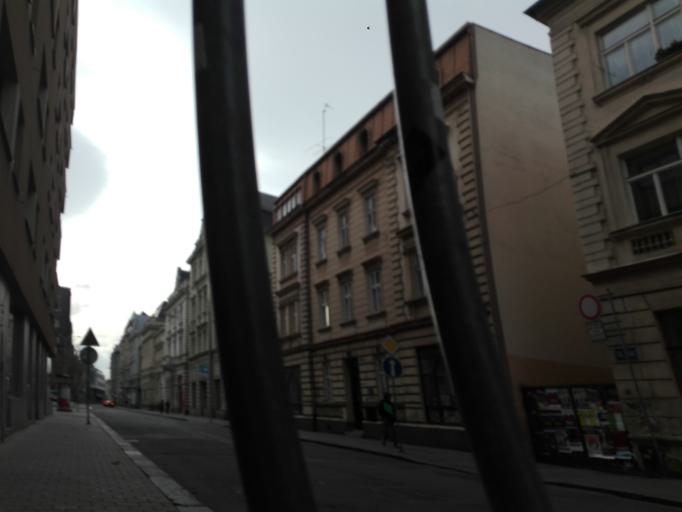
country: CZ
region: Moravskoslezsky
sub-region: Okres Ostrava-Mesto
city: Ostrava
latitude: 49.8366
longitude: 18.2895
